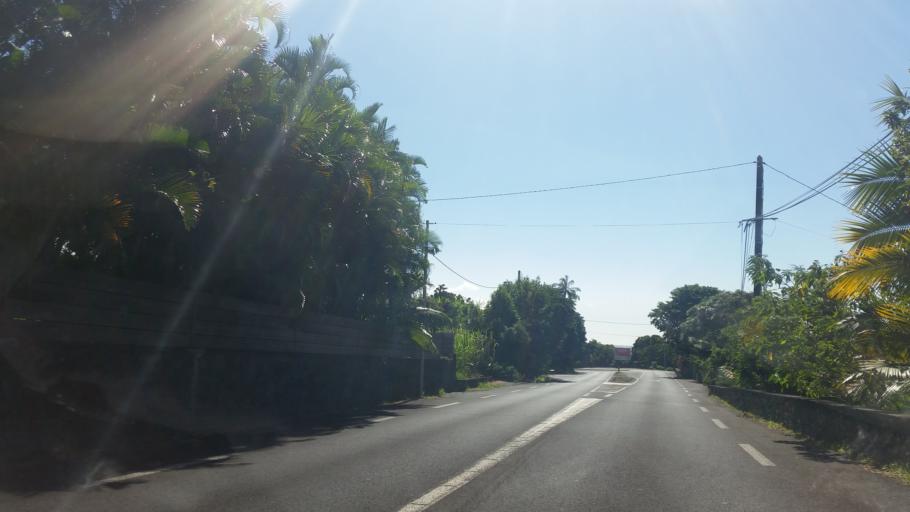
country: RE
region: Reunion
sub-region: Reunion
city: Saint-Benoit
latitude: -21.0844
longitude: 55.6914
